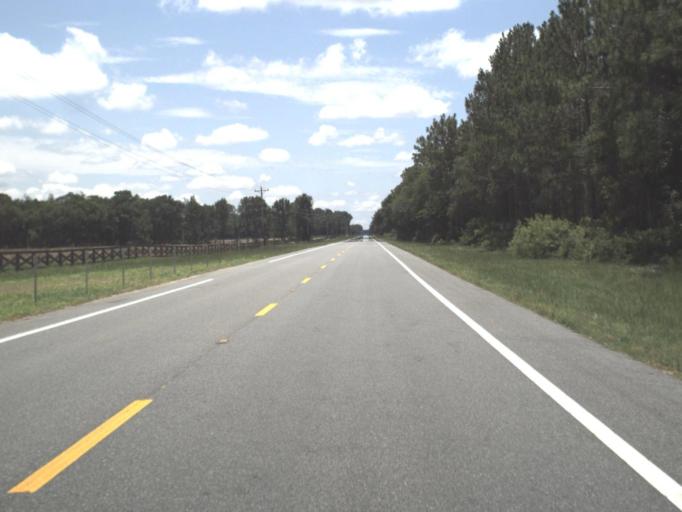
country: US
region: Florida
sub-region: Lafayette County
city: Mayo
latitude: 29.9149
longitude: -82.9517
